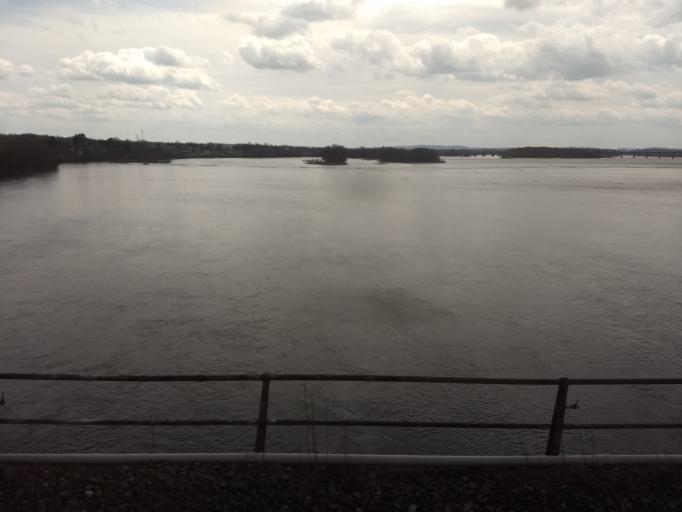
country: US
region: Pennsylvania
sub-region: Perry County
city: Marysville
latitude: 40.3345
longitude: -76.9066
